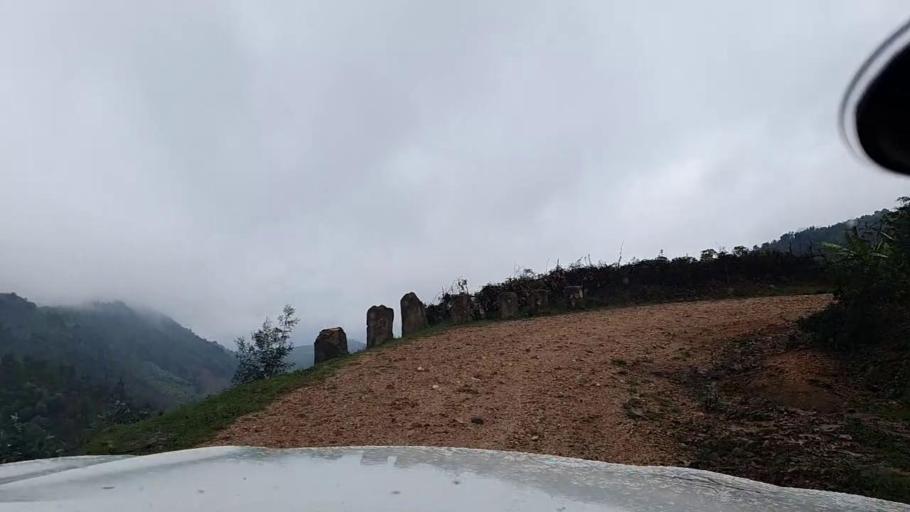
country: RW
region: Western Province
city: Kibuye
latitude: -2.1370
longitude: 29.4589
